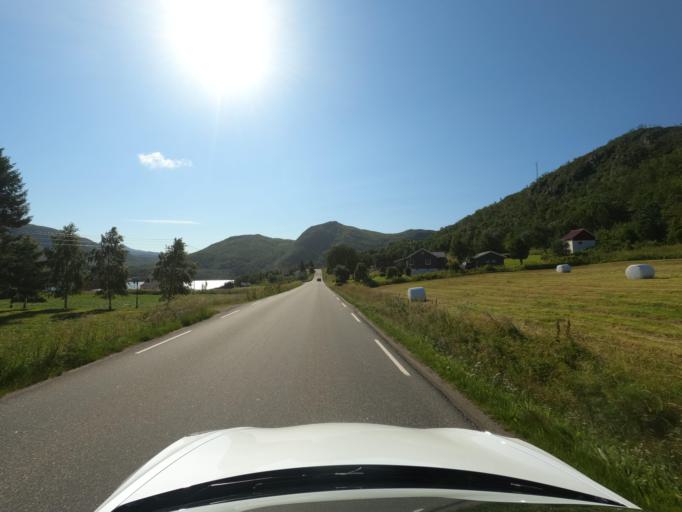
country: NO
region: Nordland
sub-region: Lodingen
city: Lodingen
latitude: 68.5691
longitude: 15.7977
